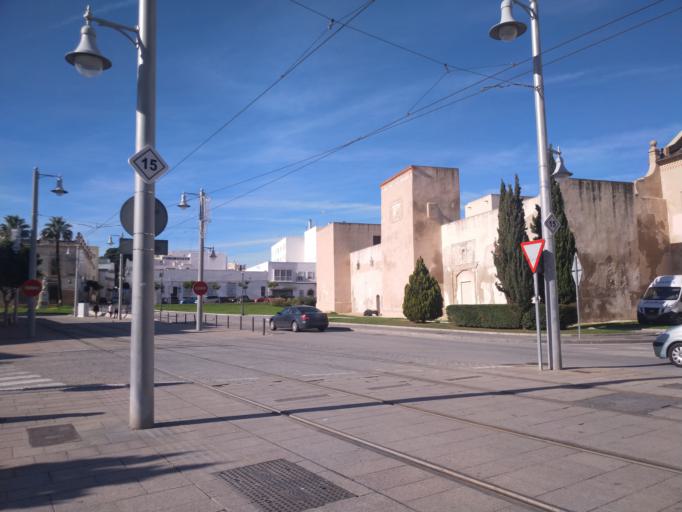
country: ES
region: Andalusia
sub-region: Provincia de Cadiz
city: San Fernando
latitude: 36.4677
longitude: -6.1913
